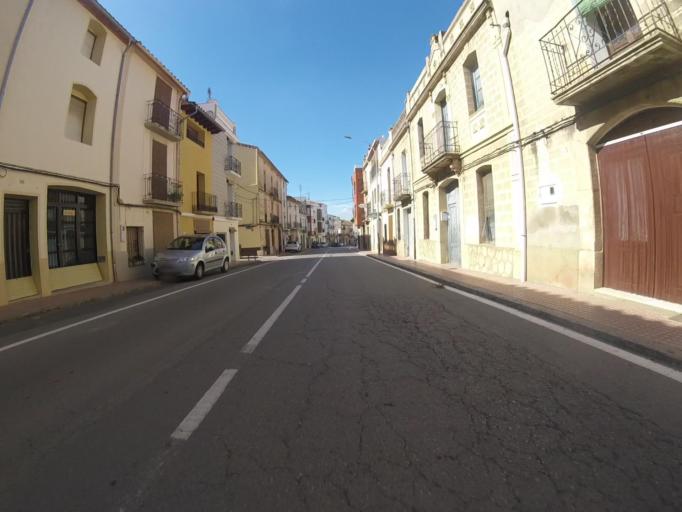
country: ES
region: Valencia
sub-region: Provincia de Castello
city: Albocasser
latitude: 40.3569
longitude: 0.0270
